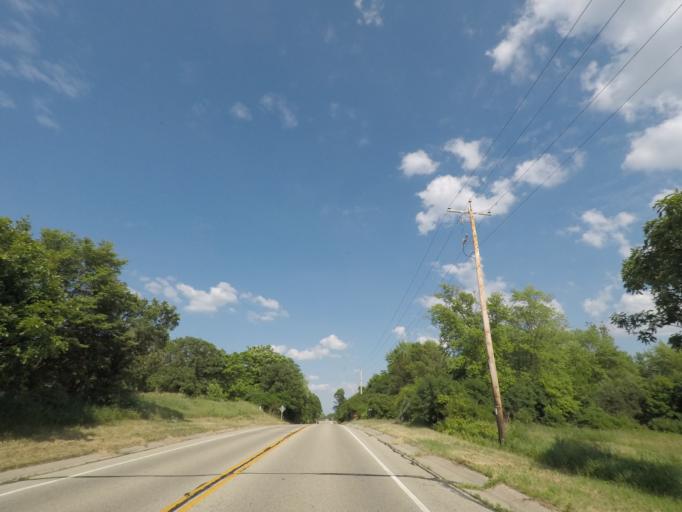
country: US
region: Wisconsin
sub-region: Walworth County
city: East Troy
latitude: 42.7932
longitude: -88.4903
